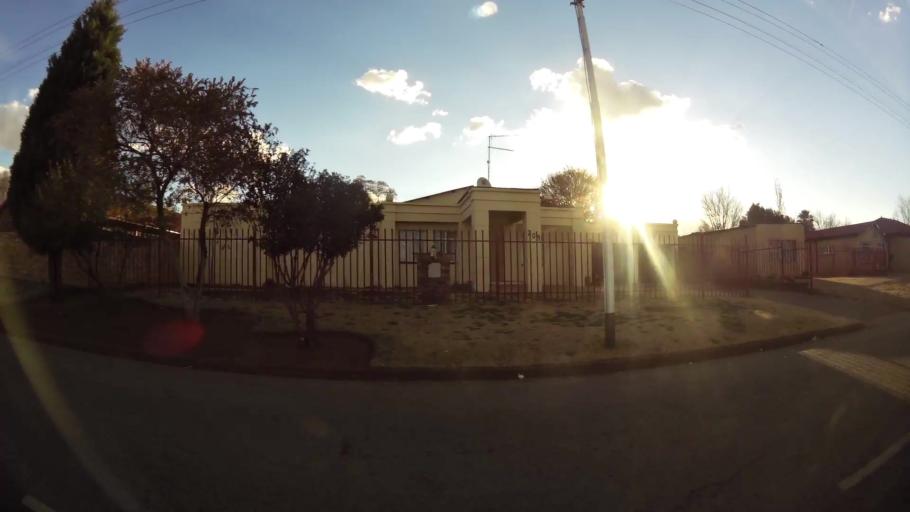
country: ZA
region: North-West
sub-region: Dr Kenneth Kaunda District Municipality
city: Potchefstroom
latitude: -26.7279
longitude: 27.1000
